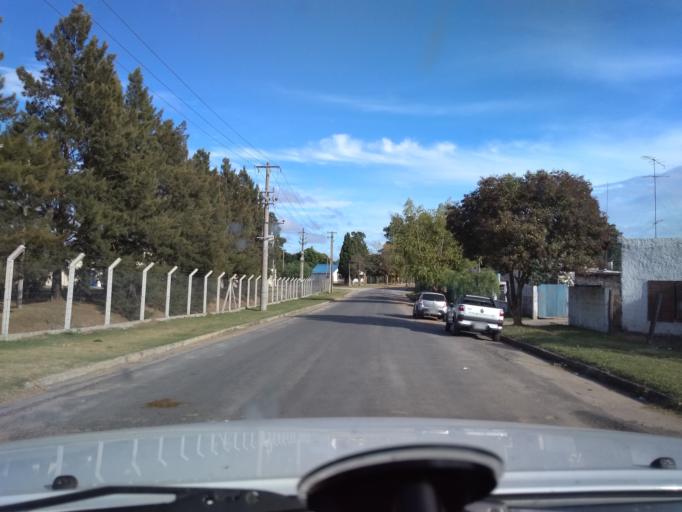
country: UY
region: Florida
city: Florida
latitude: -34.1074
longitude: -56.2156
